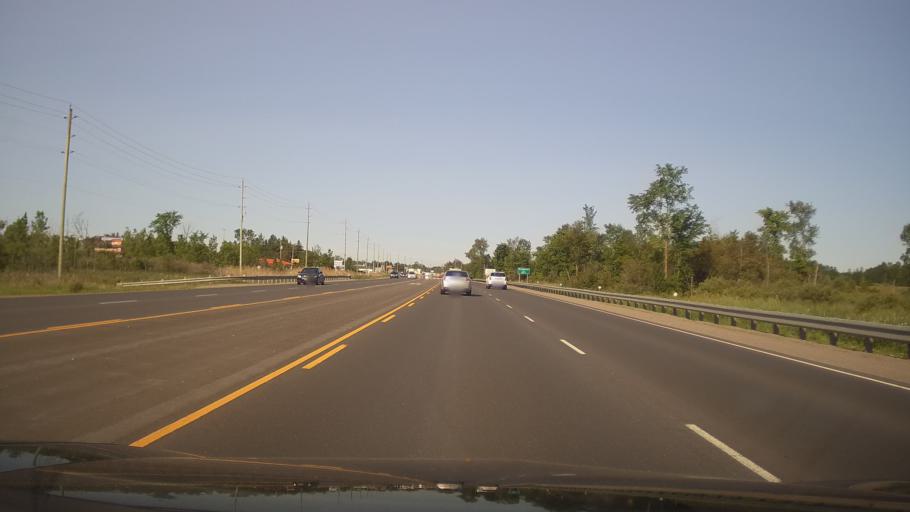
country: CA
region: Ontario
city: Peterborough
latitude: 44.3059
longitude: -78.2394
